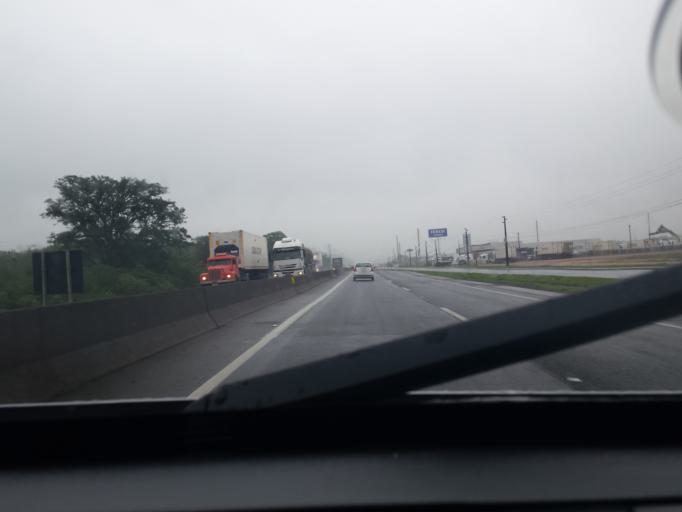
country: BR
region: Santa Catarina
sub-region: Itajai
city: Itajai
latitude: -26.9145
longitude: -48.7112
